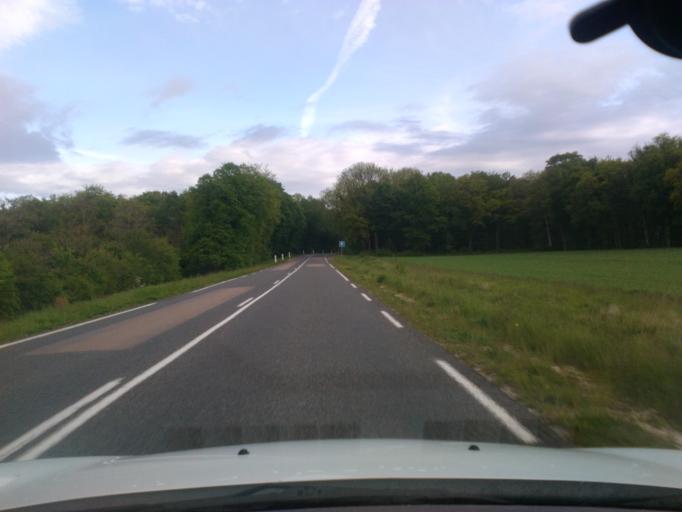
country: FR
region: Champagne-Ardenne
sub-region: Departement de la Haute-Marne
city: Lavilleneuve-au-Roi
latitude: 48.2056
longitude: 4.9347
